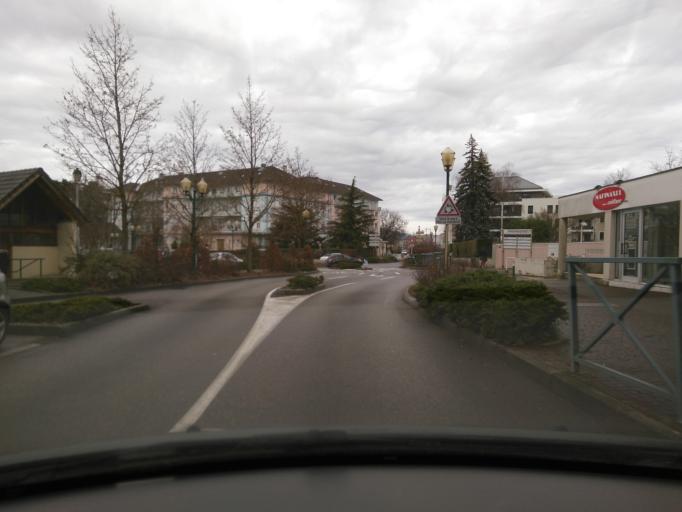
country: FR
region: Rhone-Alpes
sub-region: Departement de la Haute-Savoie
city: Saint-Julien-en-Genevois
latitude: 46.1453
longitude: 6.0807
